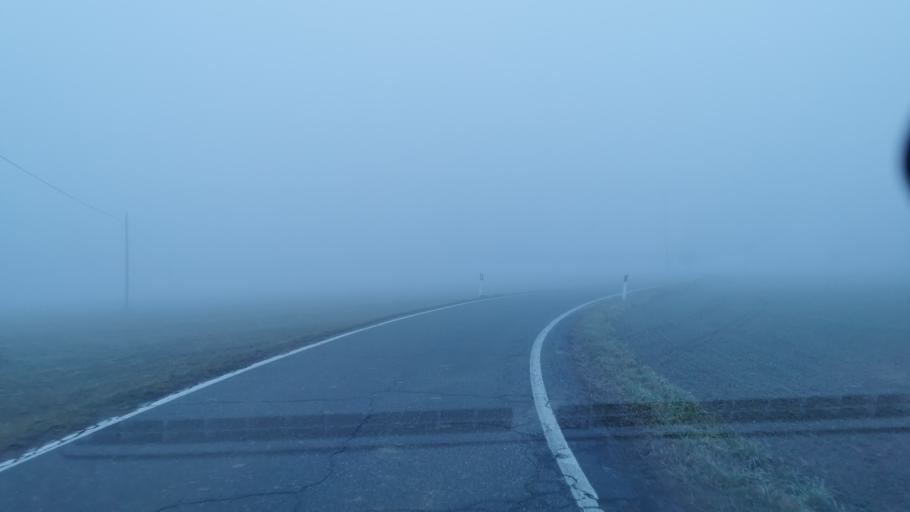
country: IT
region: Piedmont
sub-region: Provincia di Torino
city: Leini
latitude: 45.1995
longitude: 7.7417
